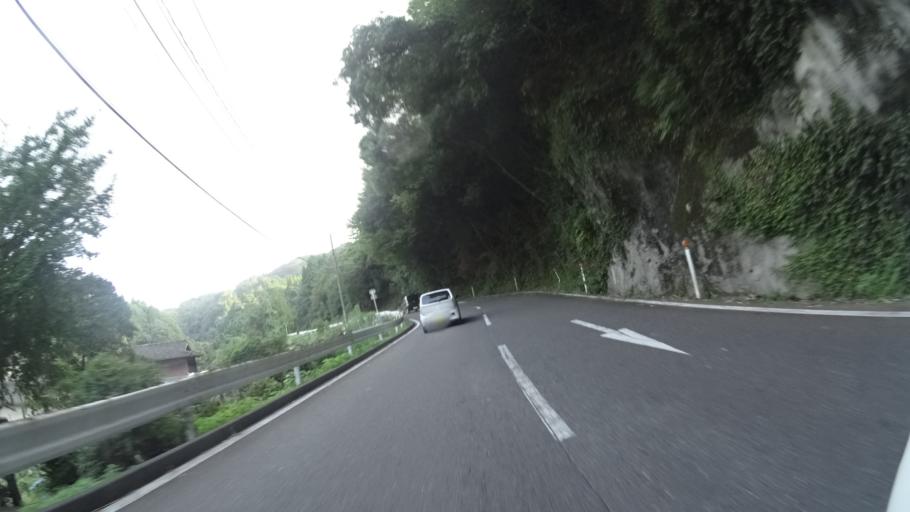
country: JP
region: Oita
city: Beppu
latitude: 33.3604
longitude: 131.3962
